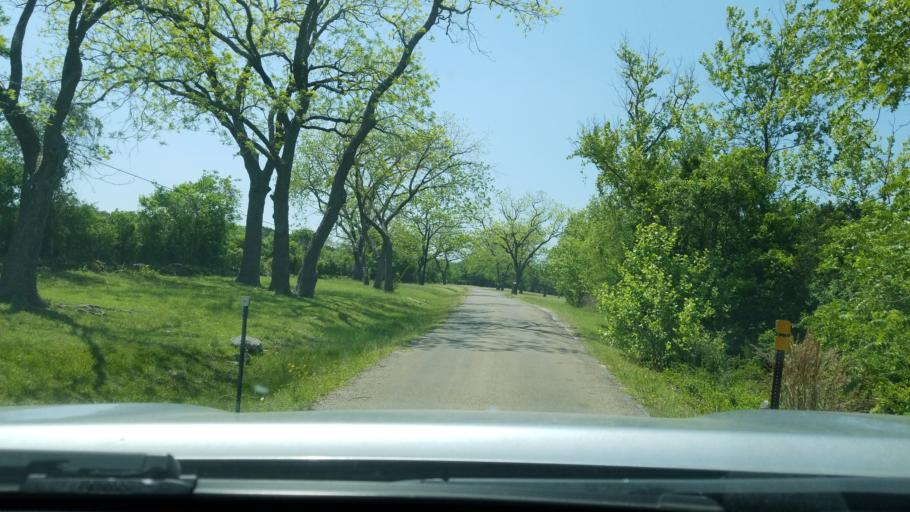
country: US
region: Texas
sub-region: Blanco County
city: Blanco
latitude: 30.0044
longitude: -98.4288
